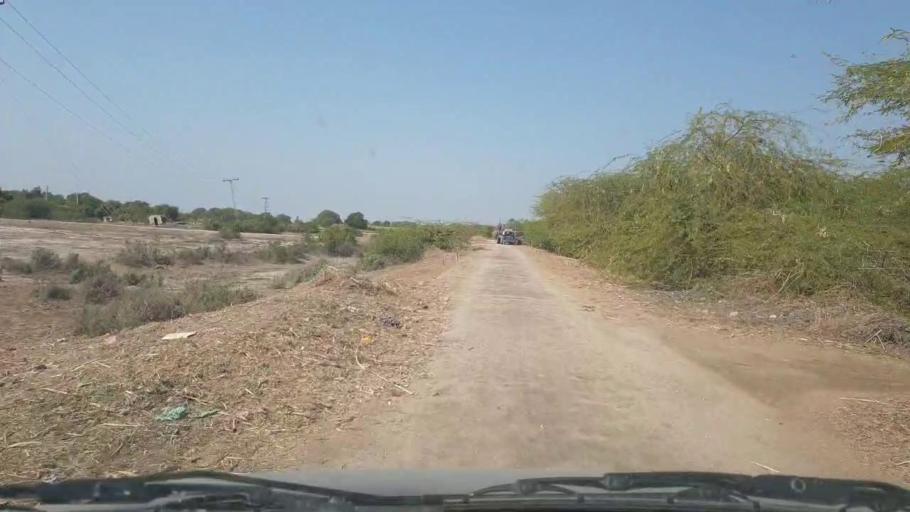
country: PK
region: Sindh
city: Samaro
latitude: 25.2280
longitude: 69.3204
